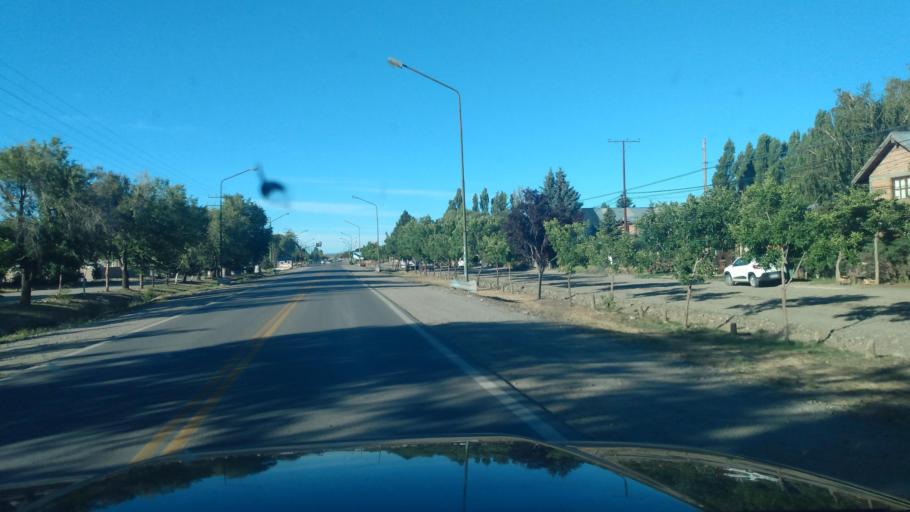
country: AR
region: Neuquen
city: Junin de los Andes
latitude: -39.9564
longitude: -71.0781
